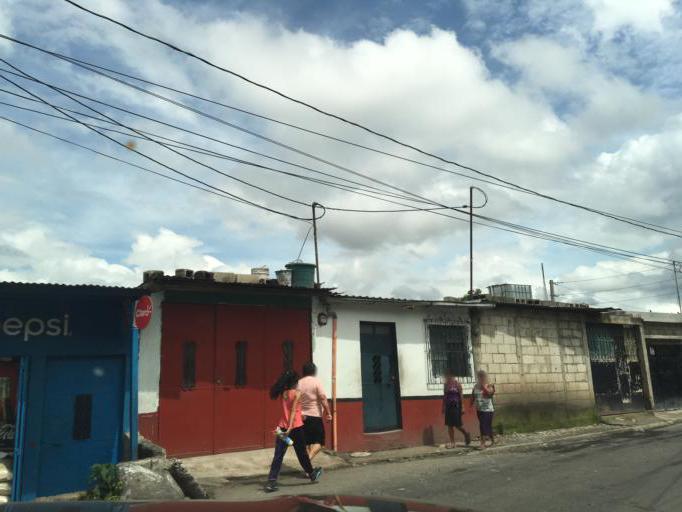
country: GT
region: Guatemala
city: Villa Nueva
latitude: 14.5058
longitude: -90.5891
